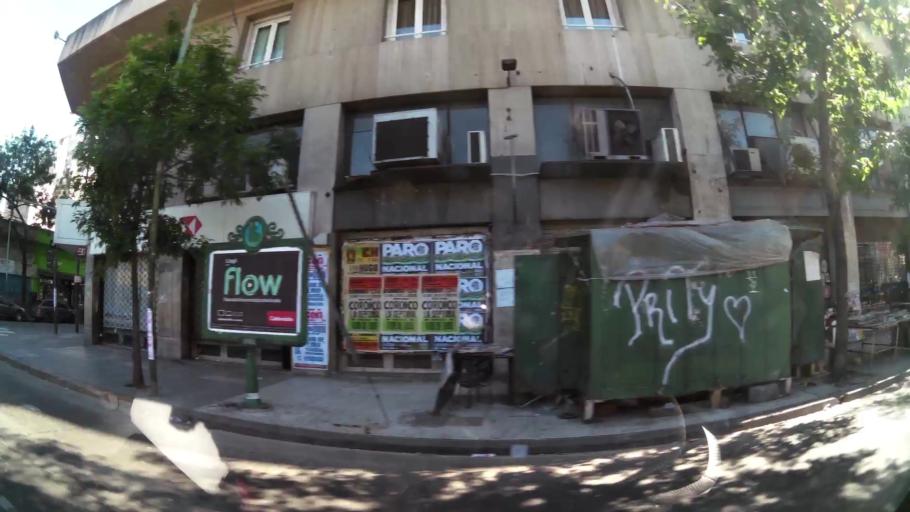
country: AR
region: Buenos Aires F.D.
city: Buenos Aires
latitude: -34.6279
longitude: -58.3826
